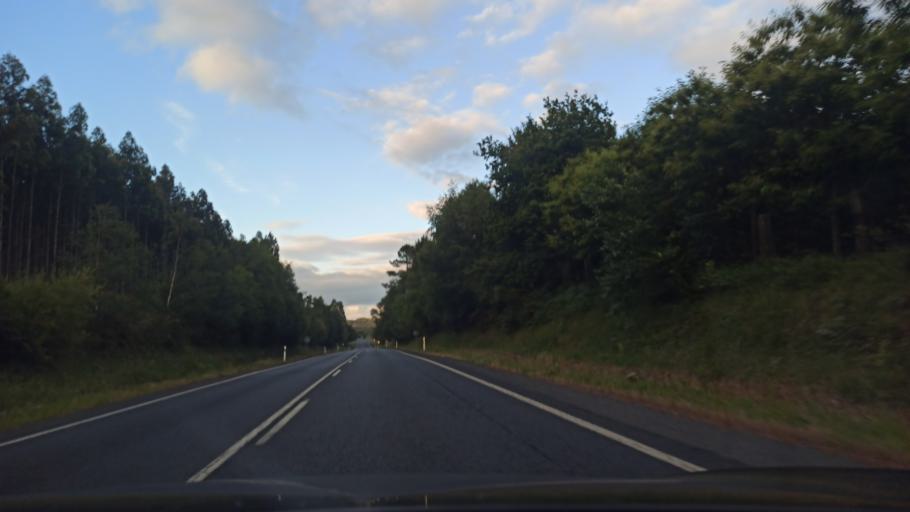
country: ES
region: Galicia
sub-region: Provincia da Coruna
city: Santiso
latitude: 42.7643
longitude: -8.0037
